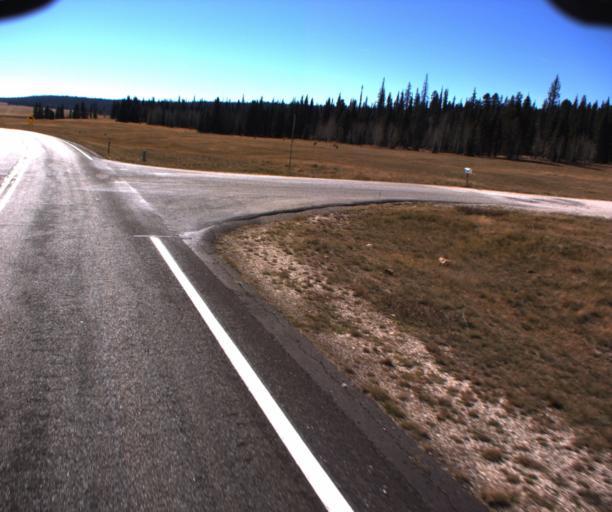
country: US
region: Arizona
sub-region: Coconino County
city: Grand Canyon
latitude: 36.4109
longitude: -112.1316
